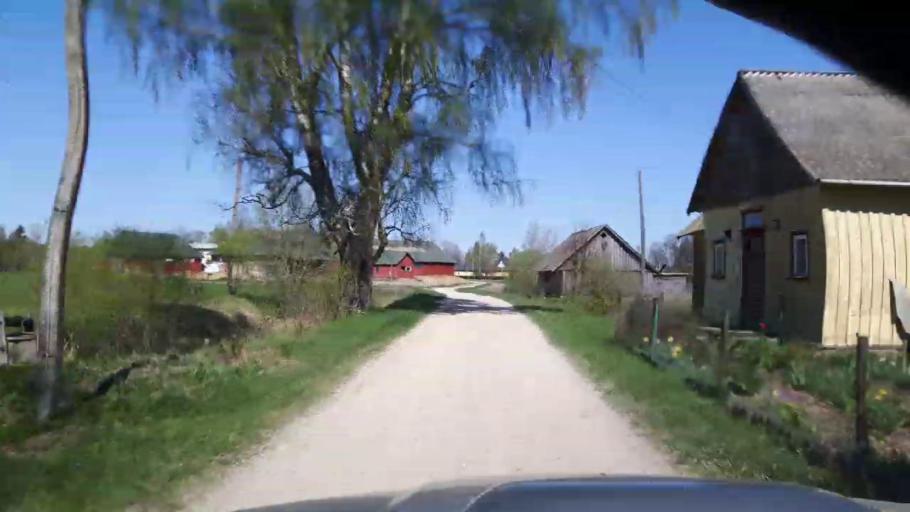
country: EE
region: Paernumaa
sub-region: Tootsi vald
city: Tootsi
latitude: 58.4776
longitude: 24.8078
